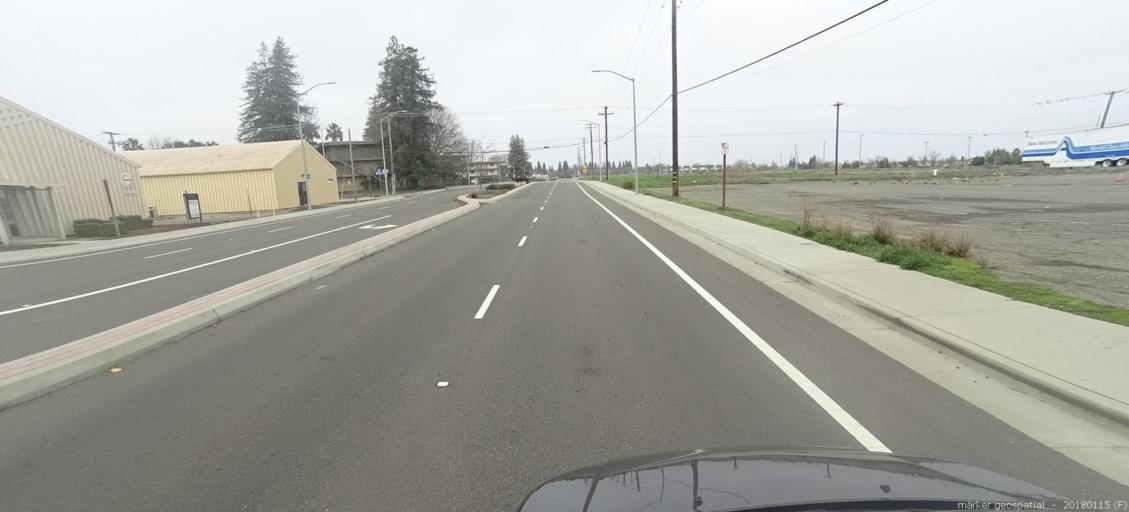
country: US
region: California
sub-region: Sacramento County
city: Rancho Cordova
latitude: 38.5695
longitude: -121.2910
